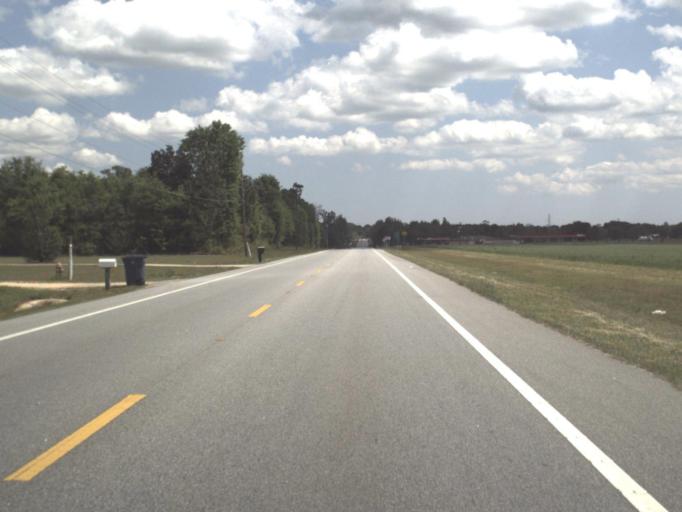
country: US
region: Florida
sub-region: Escambia County
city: Molino
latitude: 30.7349
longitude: -87.3533
